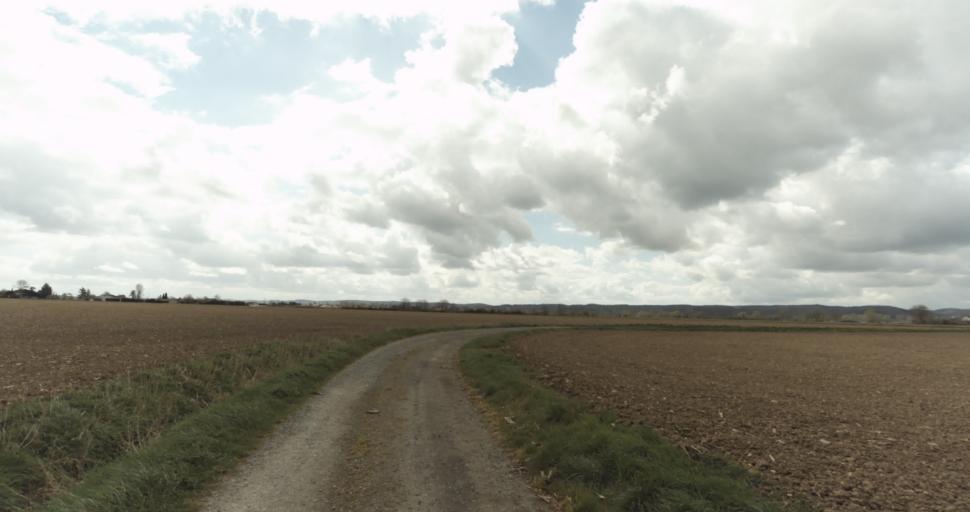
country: FR
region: Midi-Pyrenees
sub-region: Departement de la Haute-Garonne
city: Auterive
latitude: 43.3380
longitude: 1.4695
